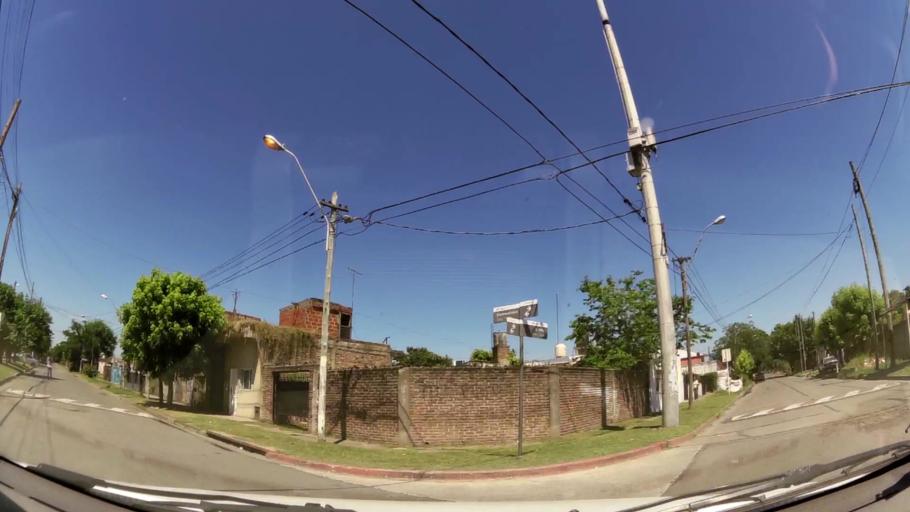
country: AR
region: Buenos Aires
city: Ituzaingo
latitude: -34.6850
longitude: -58.6606
